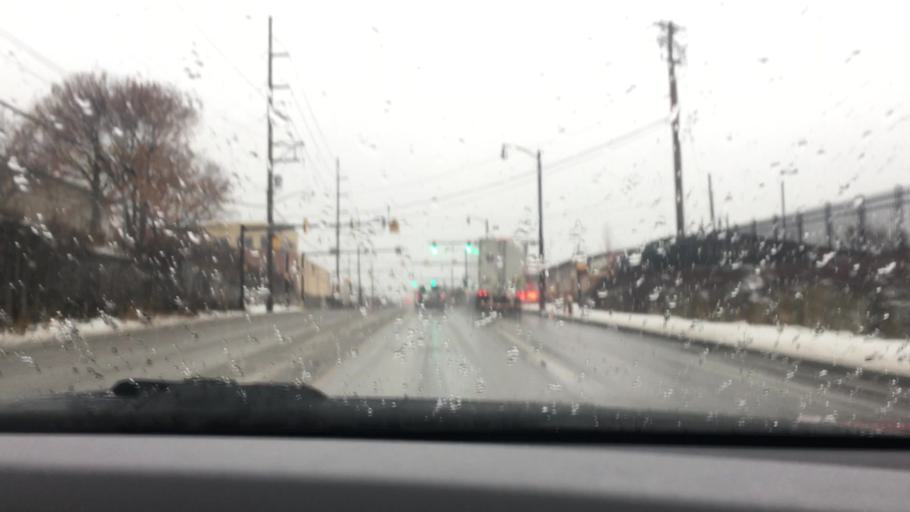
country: US
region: Pennsylvania
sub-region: Allegheny County
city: Mount Oliver
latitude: 40.4221
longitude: -79.9595
